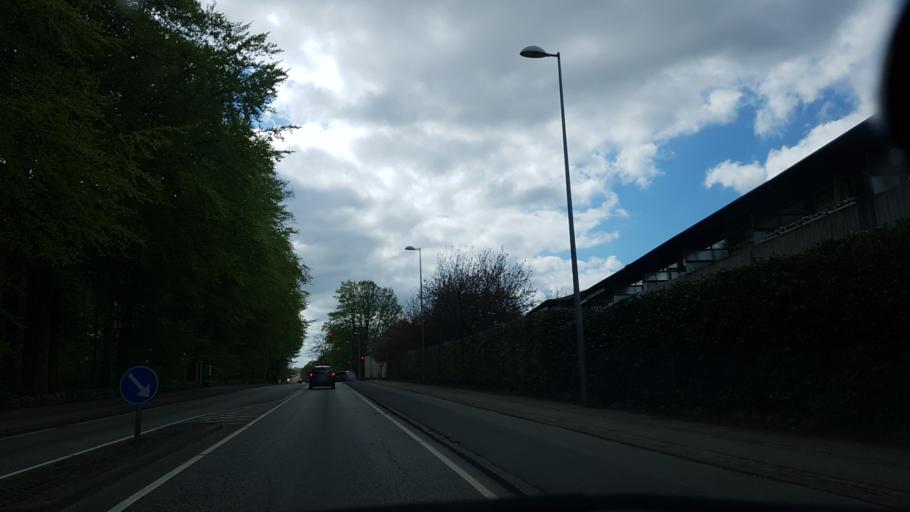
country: DK
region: Capital Region
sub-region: Horsholm Kommune
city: Horsholm
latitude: 55.8822
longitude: 12.5145
